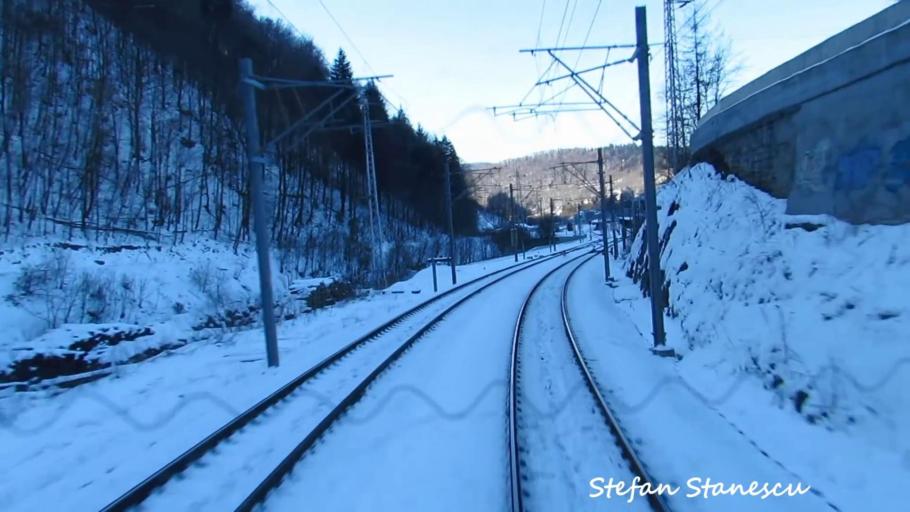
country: RO
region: Prahova
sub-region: Oras Sinaia
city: Sinaia
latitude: 45.3624
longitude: 25.5512
